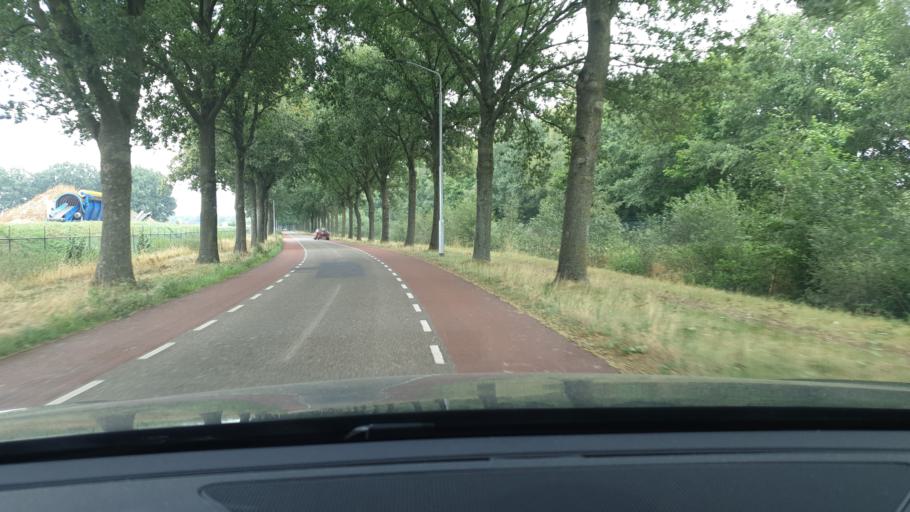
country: NL
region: North Brabant
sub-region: Gemeente Veldhoven
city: Oerle
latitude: 51.4432
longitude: 5.3611
